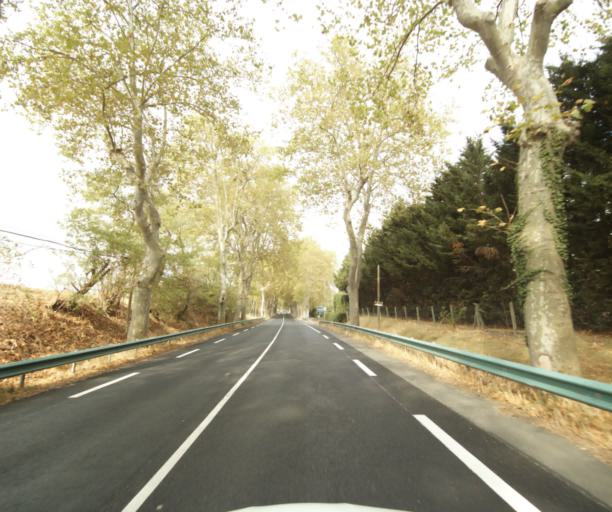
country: FR
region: Midi-Pyrenees
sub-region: Departement de la Haute-Garonne
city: Villefranche-de-Lauragais
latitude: 43.4141
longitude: 1.7000
